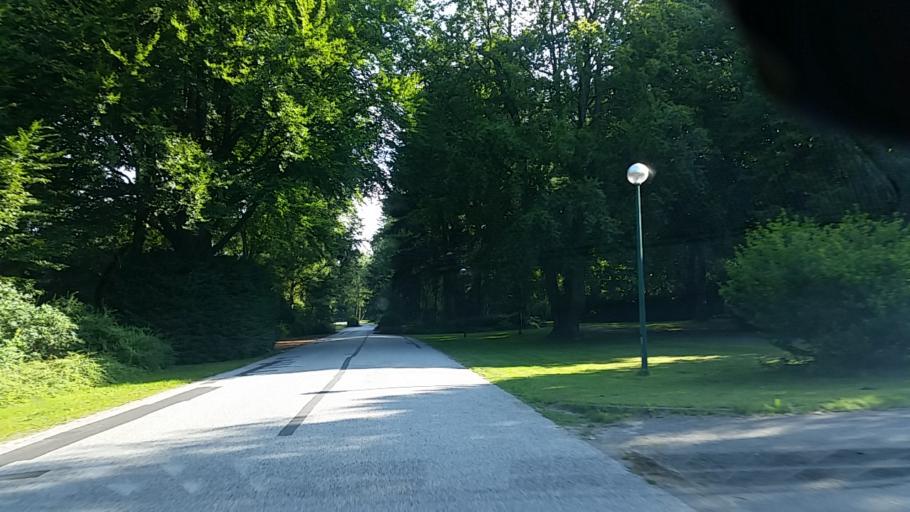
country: DE
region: Hamburg
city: Wandsbek
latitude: 53.5548
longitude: 10.1230
